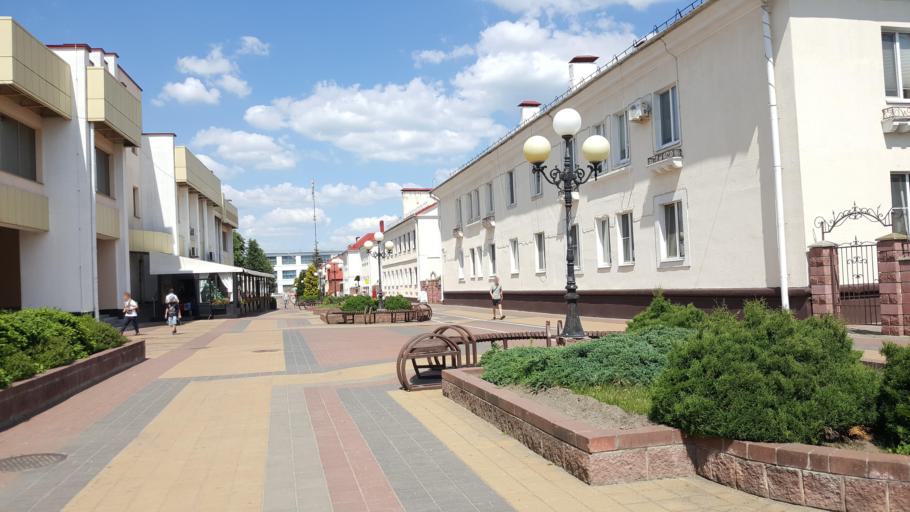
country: BY
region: Brest
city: Kobryn
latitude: 52.2098
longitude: 24.3559
